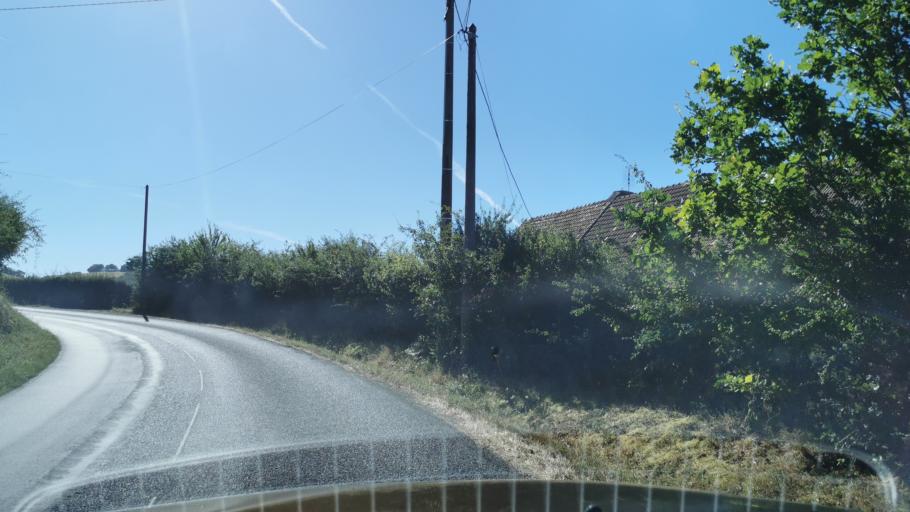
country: FR
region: Bourgogne
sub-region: Departement de Saone-et-Loire
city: Marmagne
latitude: 46.8045
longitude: 4.3388
